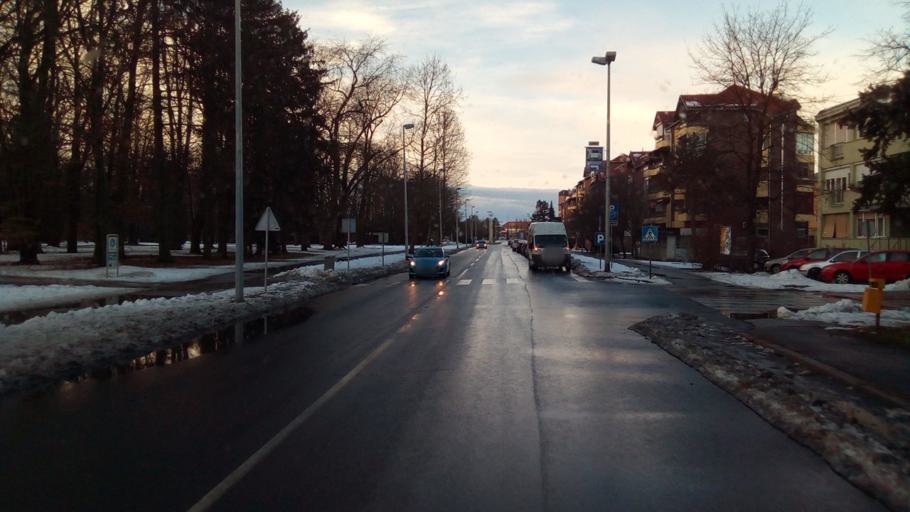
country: HR
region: Medimurska
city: Cakovec
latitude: 46.3905
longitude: 16.4315
